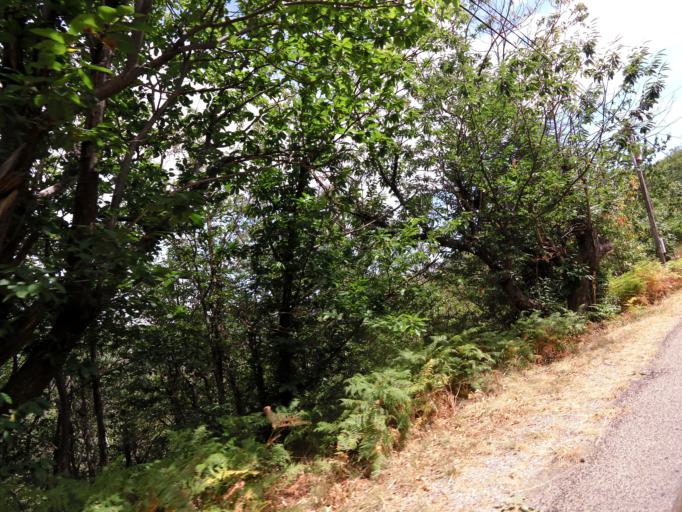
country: FR
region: Languedoc-Roussillon
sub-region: Departement du Gard
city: Le Vigan
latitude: 44.0267
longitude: 3.6215
